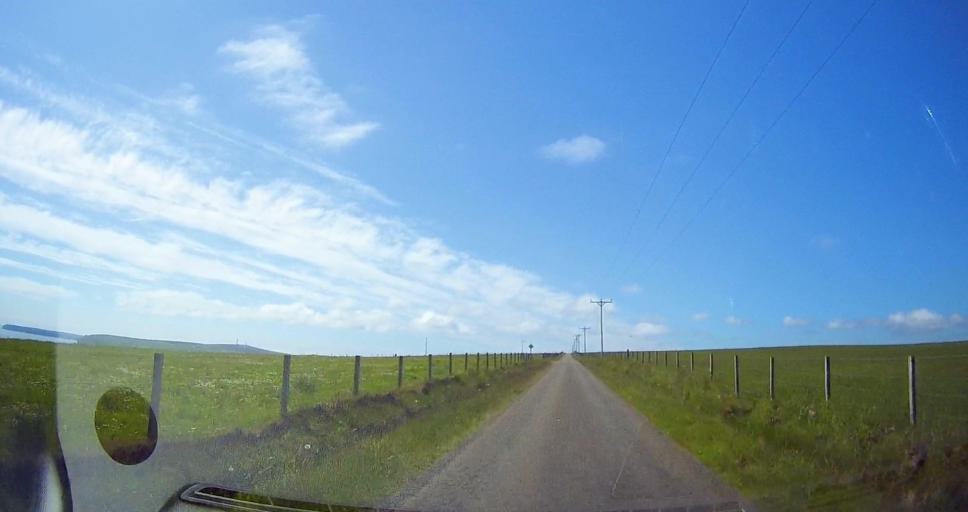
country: GB
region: Scotland
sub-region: Orkney Islands
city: Kirkwall
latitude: 58.8173
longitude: -2.9118
